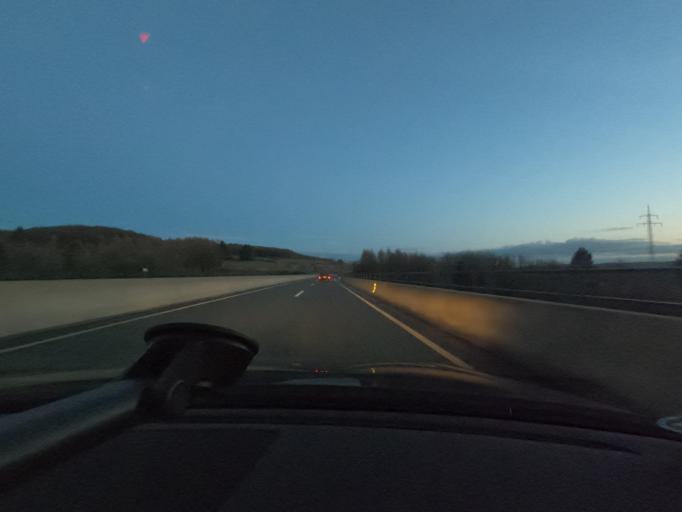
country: DE
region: Lower Saxony
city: Bad Lauterberg im Harz
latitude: 51.6069
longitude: 10.4747
